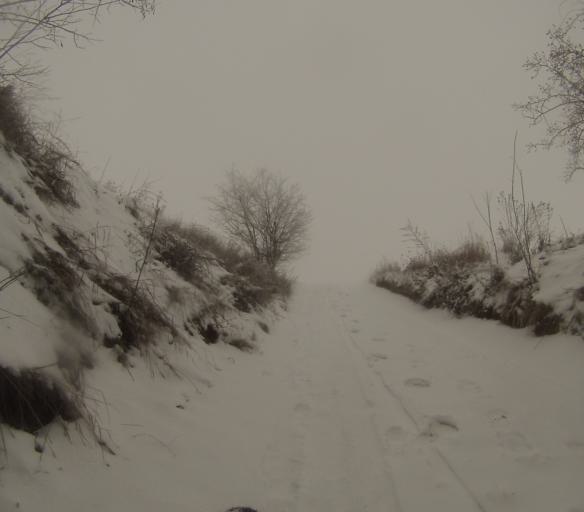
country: CZ
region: South Moravian
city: Strelice
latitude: 49.1450
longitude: 16.4946
